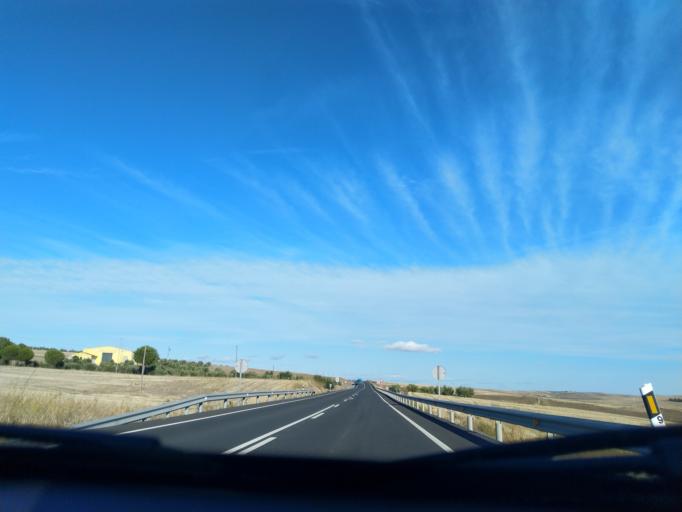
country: ES
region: Extremadura
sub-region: Provincia de Badajoz
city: Ahillones
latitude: 38.2641
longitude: -5.8566
